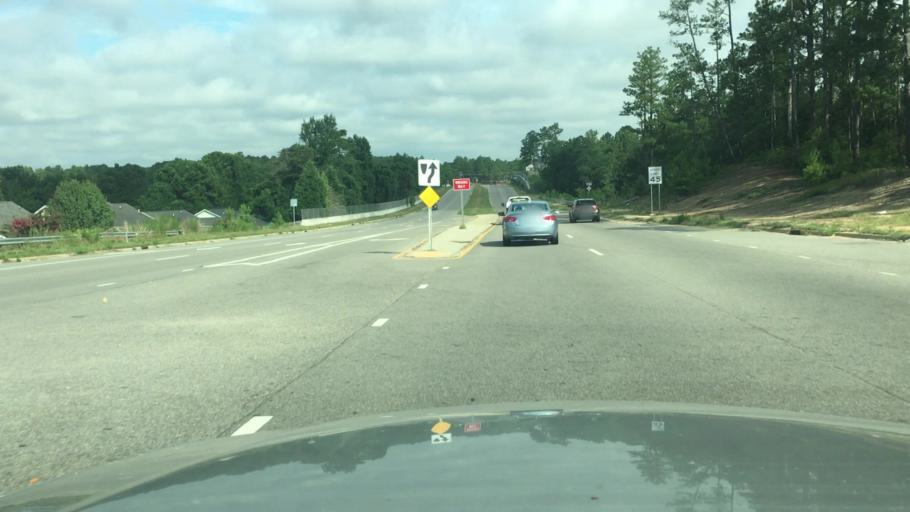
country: US
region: North Carolina
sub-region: Cumberland County
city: Hope Mills
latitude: 34.9704
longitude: -78.9155
